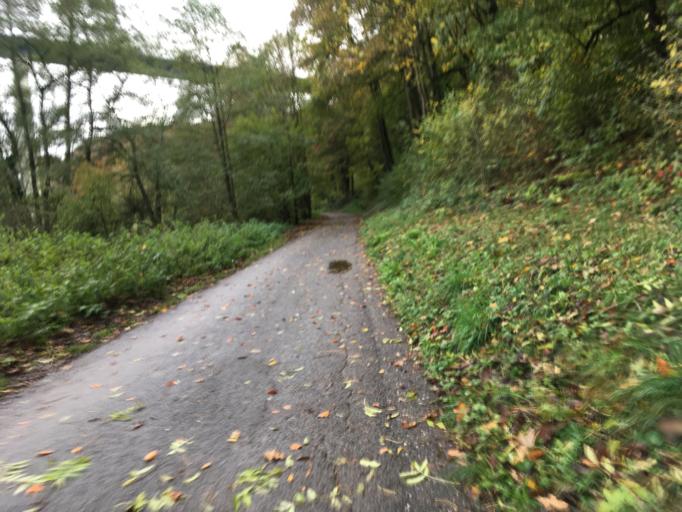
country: DE
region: Baden-Wuerttemberg
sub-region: Regierungsbezirk Stuttgart
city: Widdern
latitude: 49.3176
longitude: 9.4061
